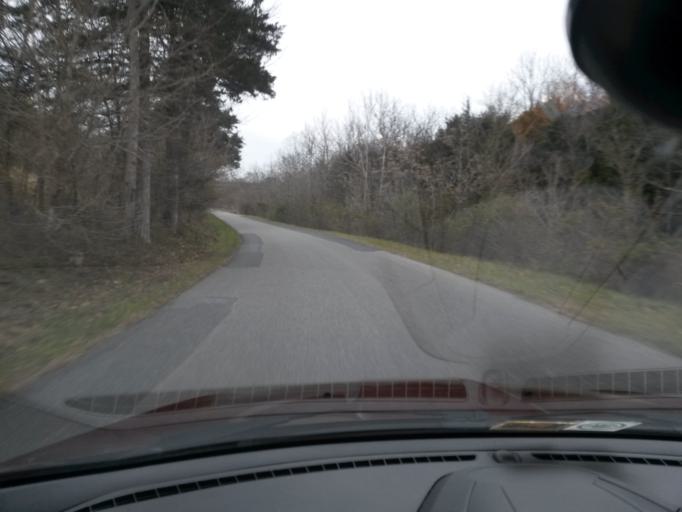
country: US
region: Virginia
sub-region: Rockbridge County
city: East Lexington
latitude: 37.7955
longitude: -79.4110
